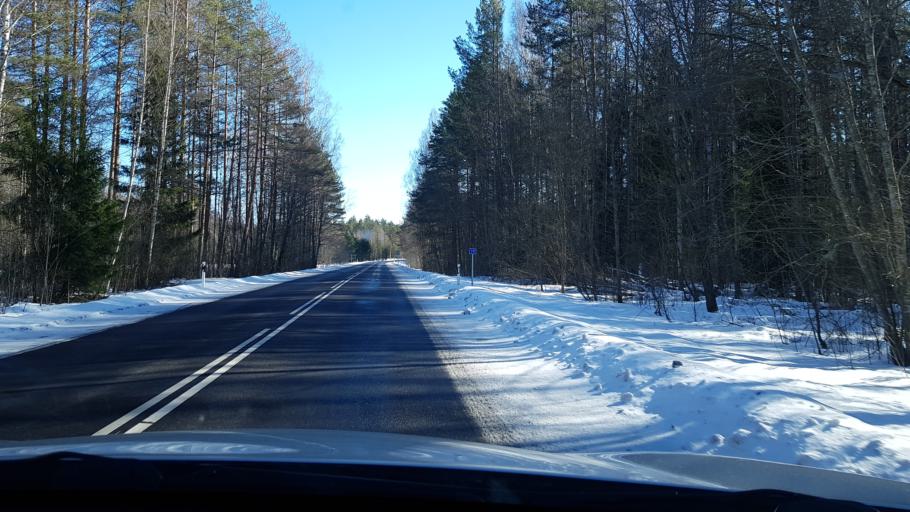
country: EE
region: Polvamaa
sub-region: Raepina vald
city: Rapina
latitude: 57.9949
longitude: 27.5559
